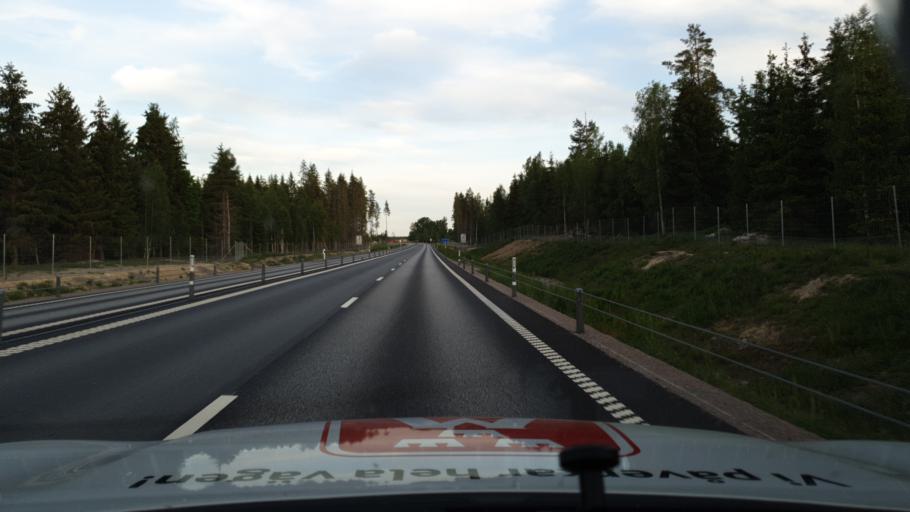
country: SE
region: OErebro
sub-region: Hallsbergs Kommun
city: Palsboda
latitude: 59.0350
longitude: 15.3577
